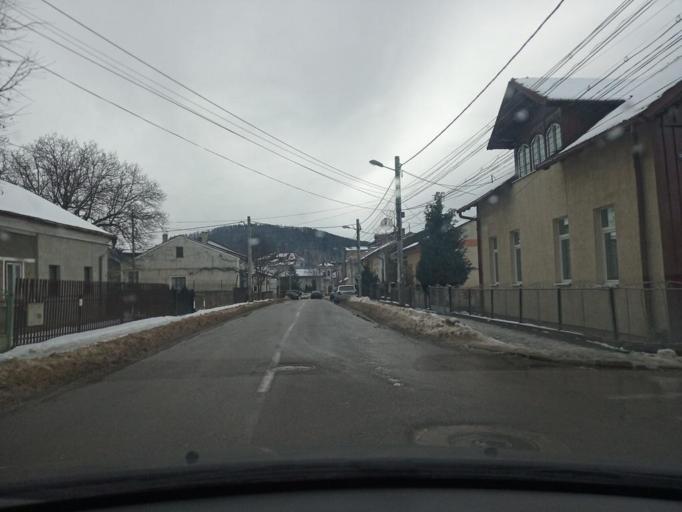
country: RO
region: Suceava
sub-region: Oras Gura Humorului
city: Gura Humorului
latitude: 47.5577
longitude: 25.8898
